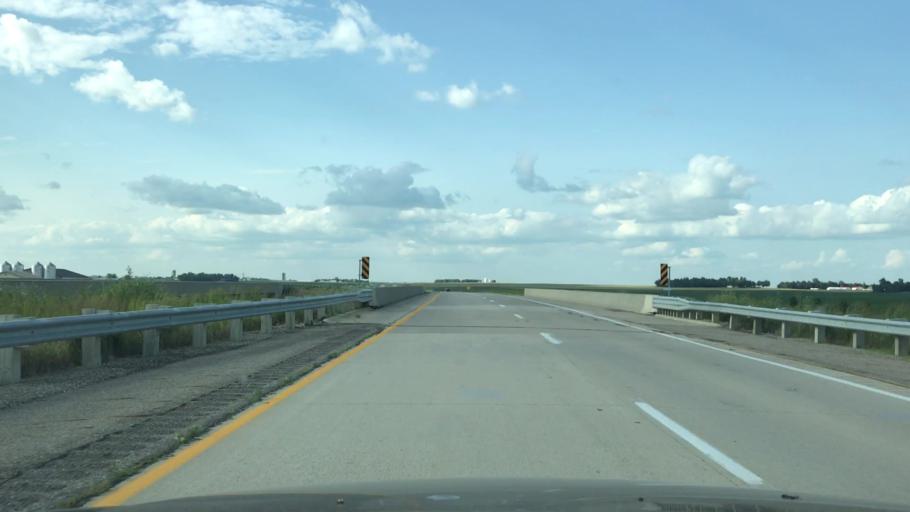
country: US
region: Iowa
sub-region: Osceola County
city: Sibley
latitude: 43.4320
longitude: -95.7135
